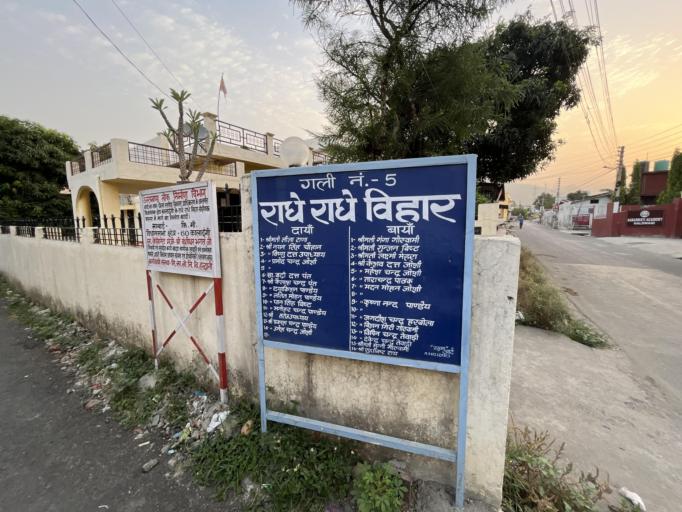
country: IN
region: Uttarakhand
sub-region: Naini Tal
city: Haldwani
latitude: 29.2314
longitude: 79.4919
